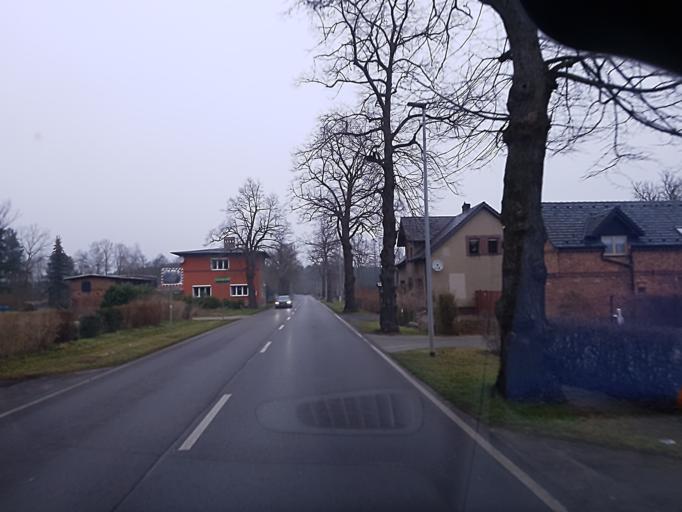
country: DE
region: Brandenburg
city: Luebben
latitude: 51.8887
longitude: 13.9011
